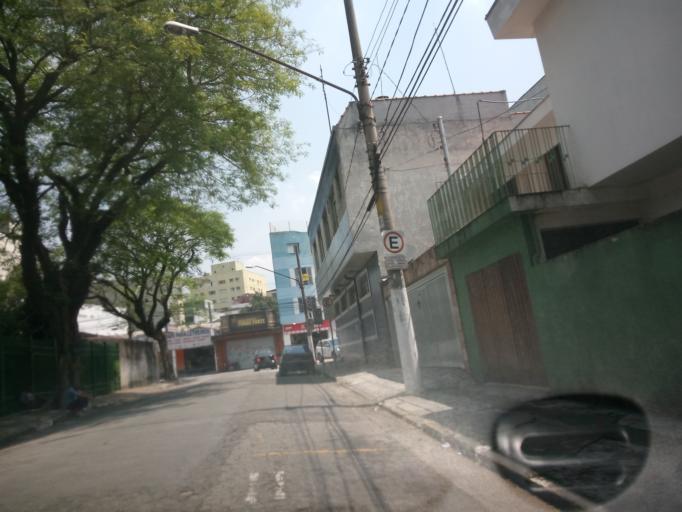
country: BR
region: Sao Paulo
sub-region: Santo Andre
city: Santo Andre
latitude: -23.6563
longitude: -46.5688
